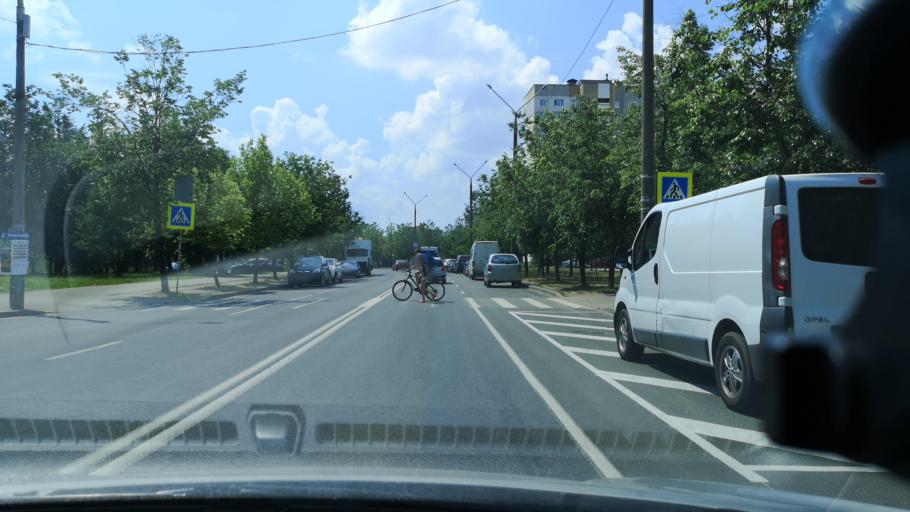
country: BY
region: Minsk
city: Lyeskawka
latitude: 53.9414
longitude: 27.6975
